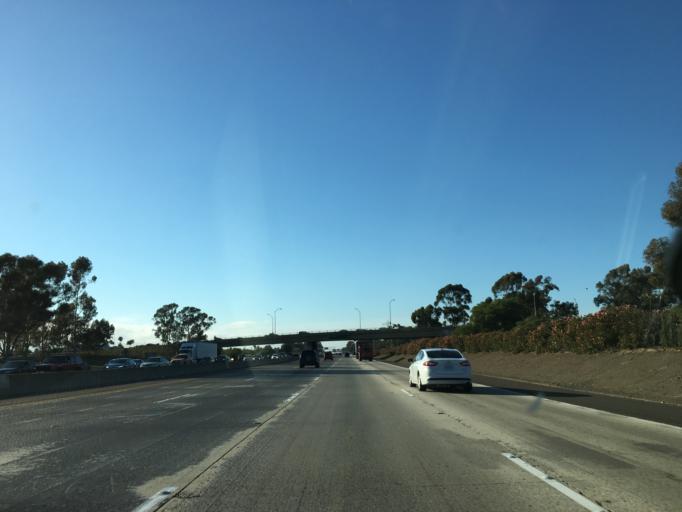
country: US
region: California
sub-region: San Diego County
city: San Diego
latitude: 32.8198
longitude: -117.1612
